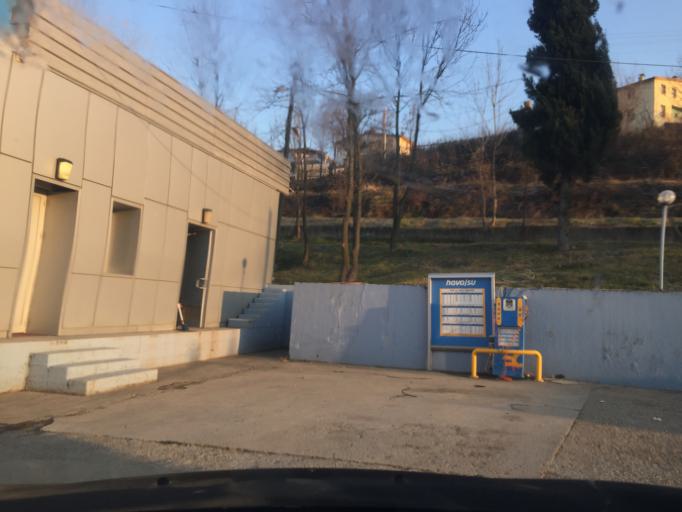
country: TR
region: Sakarya
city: Akyazi
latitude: 40.6316
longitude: 30.6365
